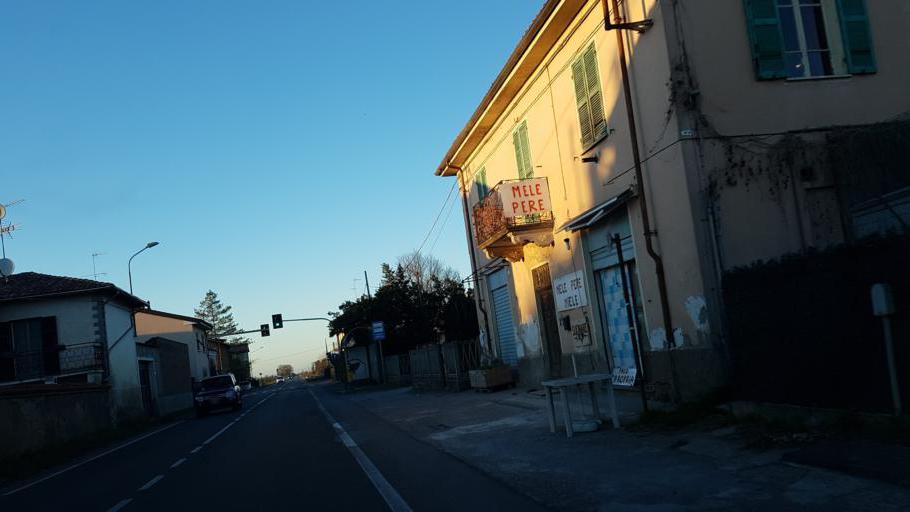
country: IT
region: Piedmont
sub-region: Provincia di Alessandria
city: Villalvernia
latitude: 44.8282
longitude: 8.8541
